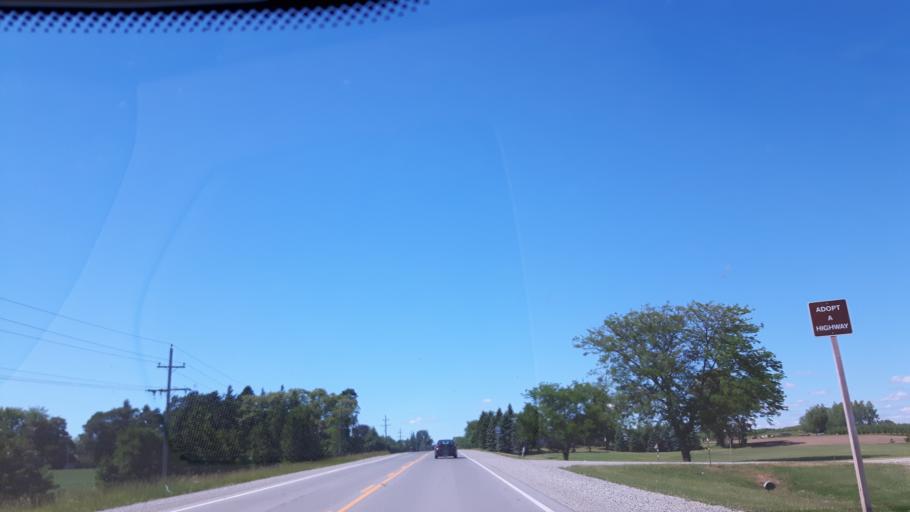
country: CA
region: Ontario
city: London
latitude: 43.1461
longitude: -81.3445
